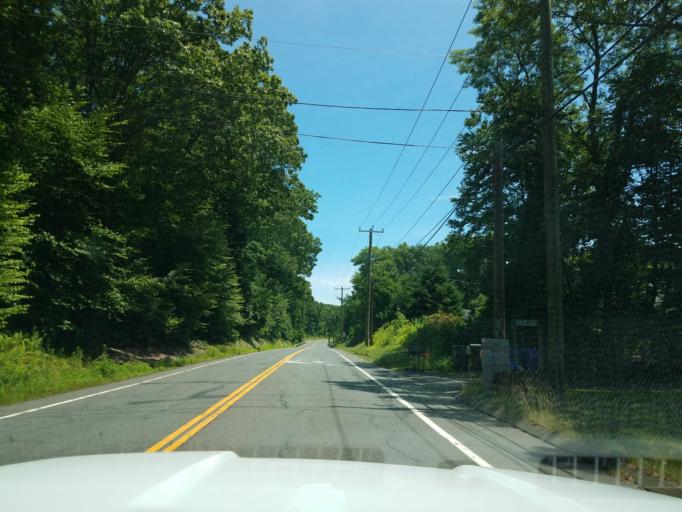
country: US
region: Connecticut
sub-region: Hartford County
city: Manchester
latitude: 41.7609
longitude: -72.4458
